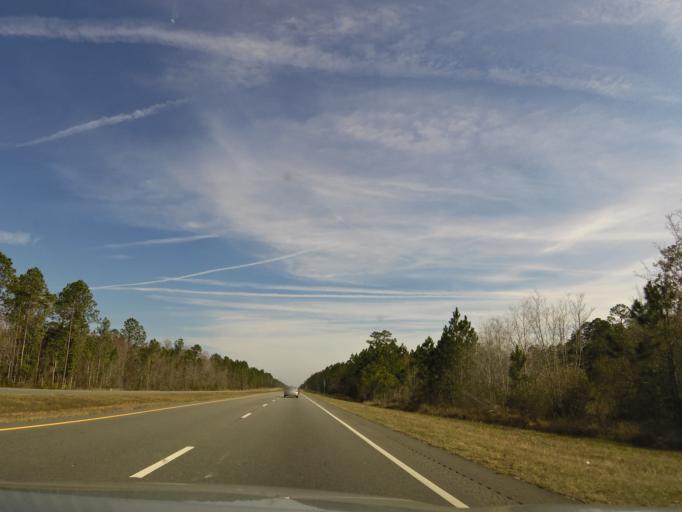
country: US
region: Georgia
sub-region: Brantley County
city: Nahunta
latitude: 31.2089
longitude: -81.9474
